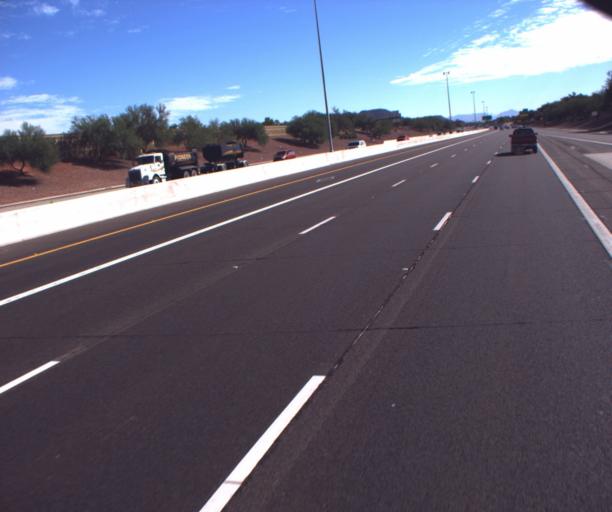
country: US
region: Arizona
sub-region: Maricopa County
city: Sun City
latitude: 33.6676
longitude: -112.2163
